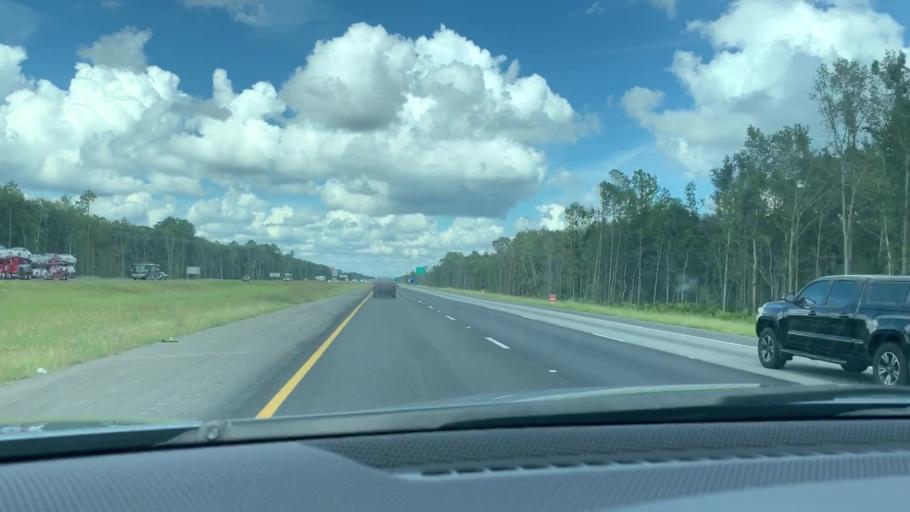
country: US
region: Georgia
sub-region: Camden County
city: Kingsland
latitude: 30.8033
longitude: -81.6614
